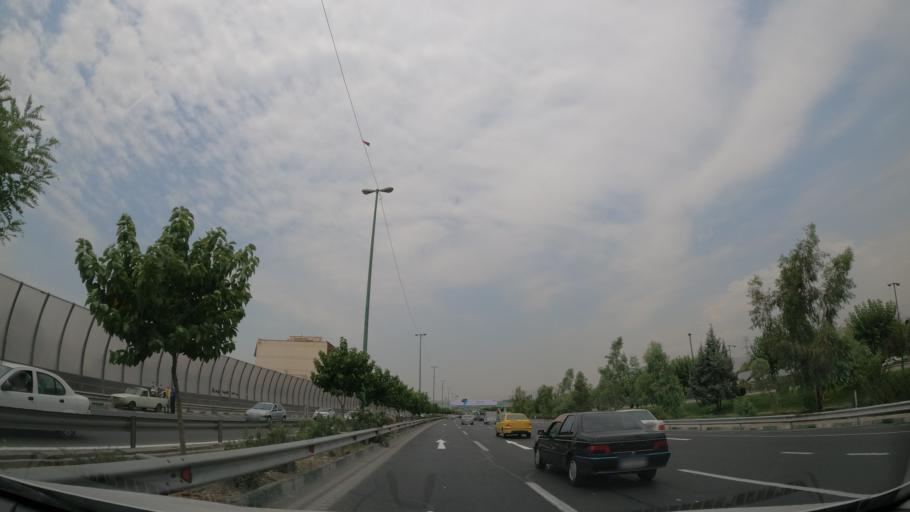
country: IR
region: Tehran
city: Tehran
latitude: 35.7390
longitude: 51.3599
